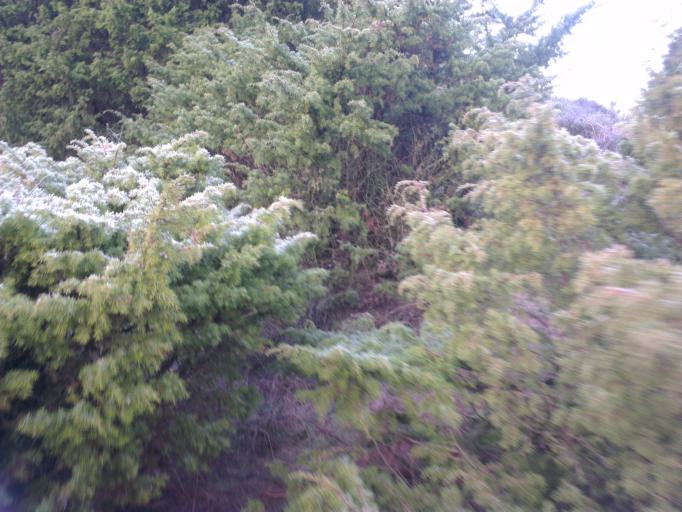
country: DK
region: Central Jutland
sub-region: Holstebro Kommune
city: Ulfborg
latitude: 56.2509
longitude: 8.4196
